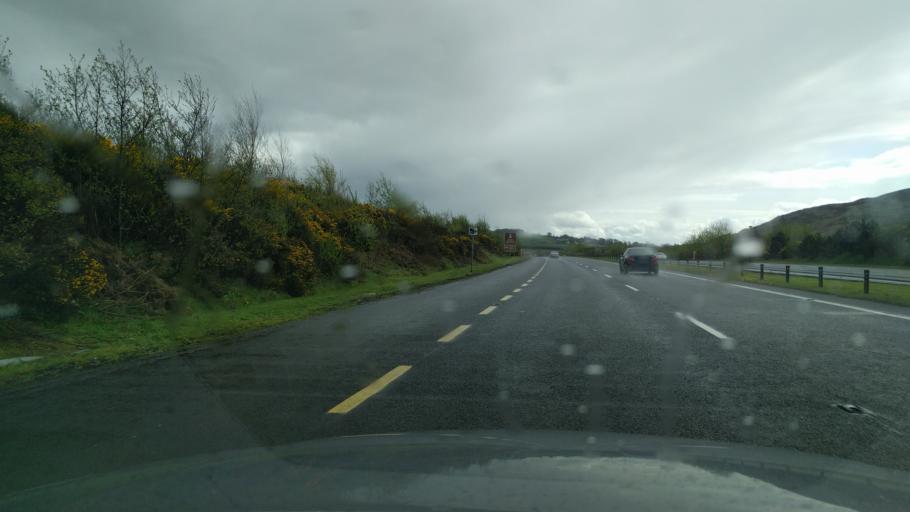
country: GB
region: Northern Ireland
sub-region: Newry and Mourne District
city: Newry
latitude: 54.1126
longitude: -6.3650
